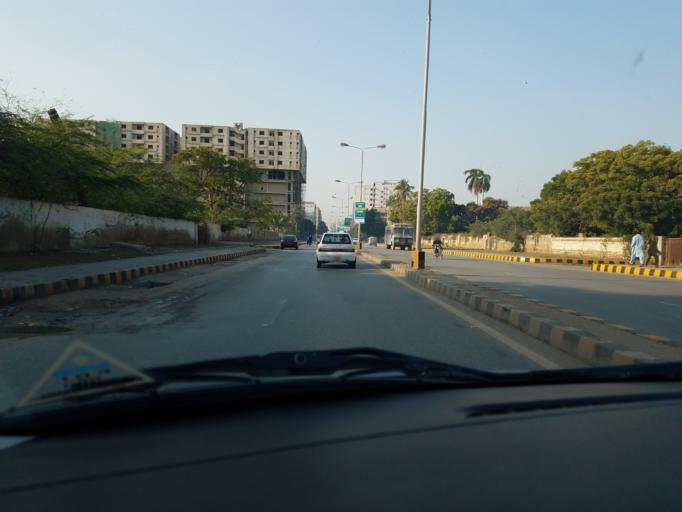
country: PK
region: Sindh
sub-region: Karachi District
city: Karachi
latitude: 24.8544
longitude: 67.0332
